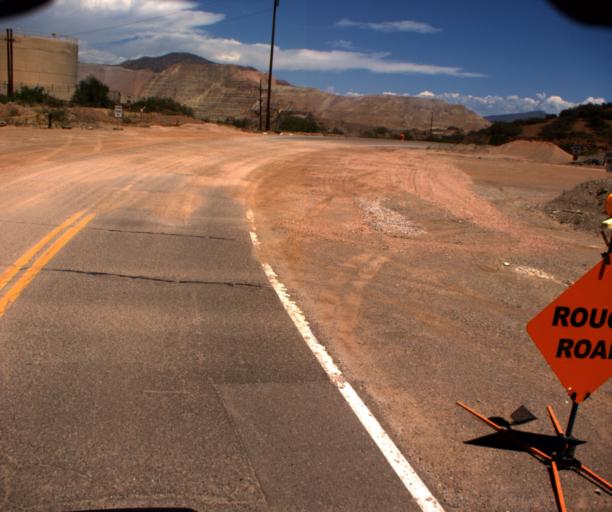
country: US
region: Arizona
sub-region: Greenlee County
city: Morenci
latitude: 33.0723
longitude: -109.3690
